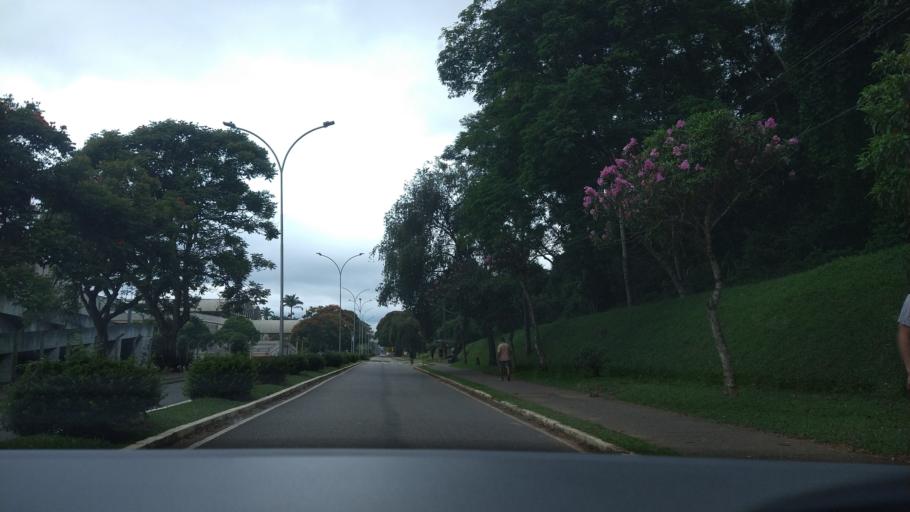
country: BR
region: Minas Gerais
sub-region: Vicosa
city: Vicosa
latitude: -20.7644
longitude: -42.8649
